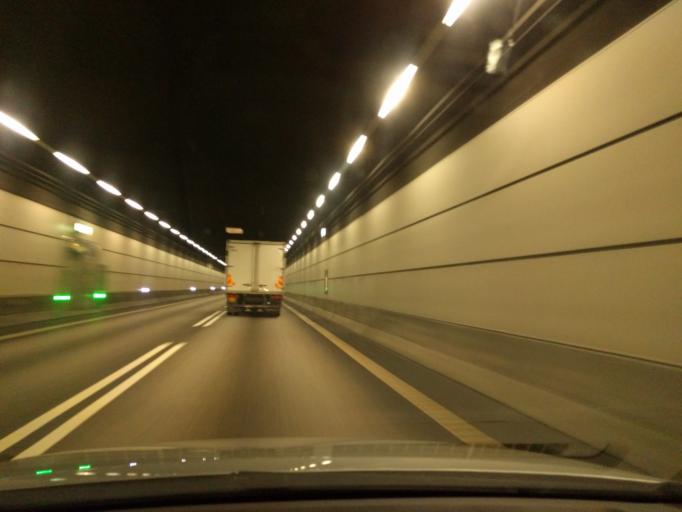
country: DK
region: Capital Region
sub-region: Dragor Kommune
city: Dragor
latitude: 55.6228
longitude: 12.6986
